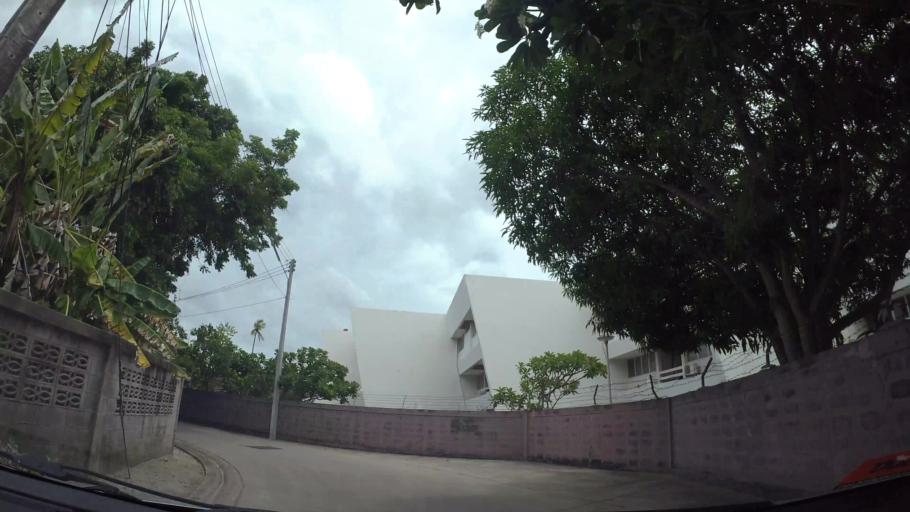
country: TH
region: Chon Buri
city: Sattahip
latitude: 12.7599
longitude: 100.8817
